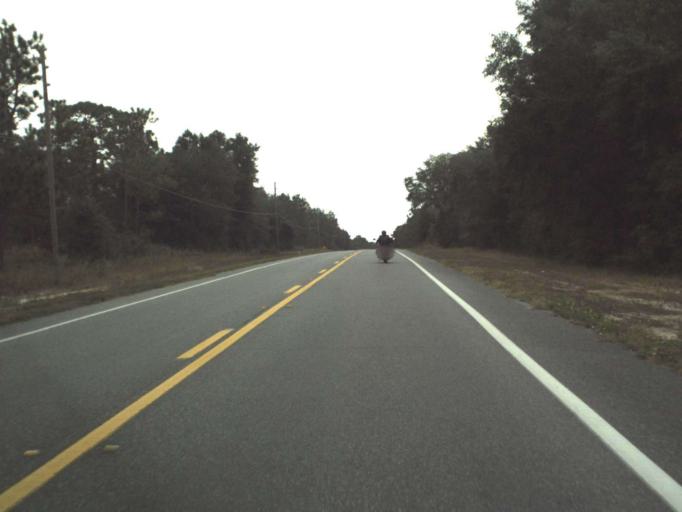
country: US
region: Florida
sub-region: Wakulla County
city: Crawfordville
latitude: 30.0646
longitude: -84.3887
